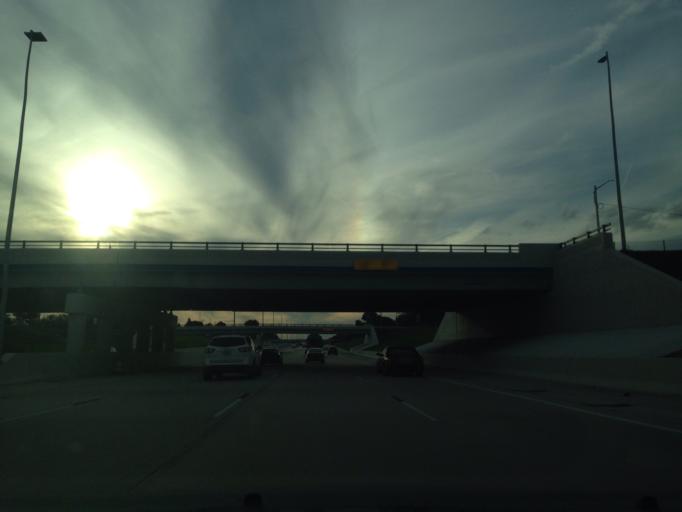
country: US
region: Michigan
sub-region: Wayne County
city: Livonia
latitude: 42.3831
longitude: -83.3528
